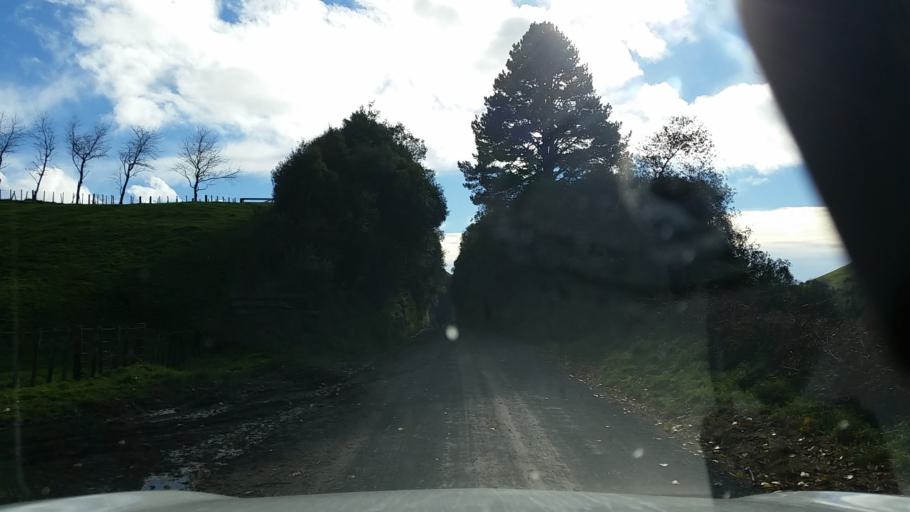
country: NZ
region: Bay of Plenty
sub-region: Rotorua District
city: Rotorua
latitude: -38.3816
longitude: 176.2016
